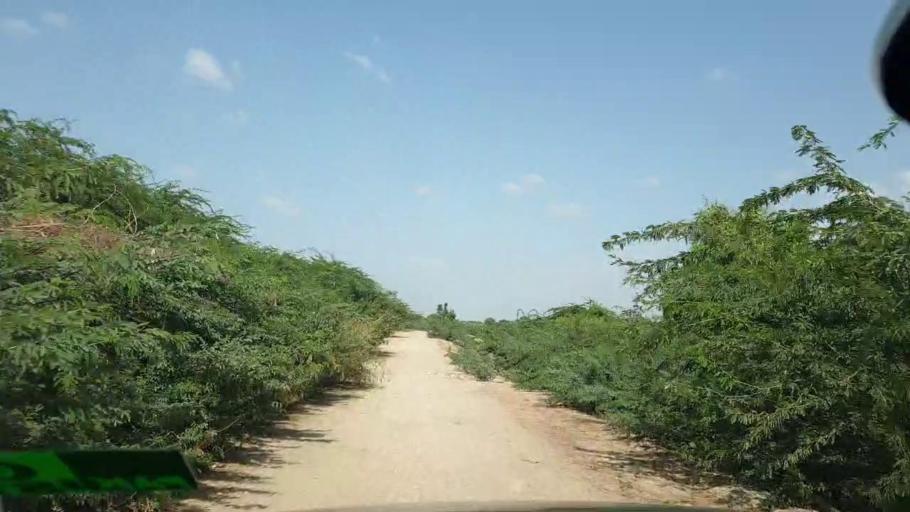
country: PK
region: Sindh
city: Naukot
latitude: 24.6442
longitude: 69.2283
